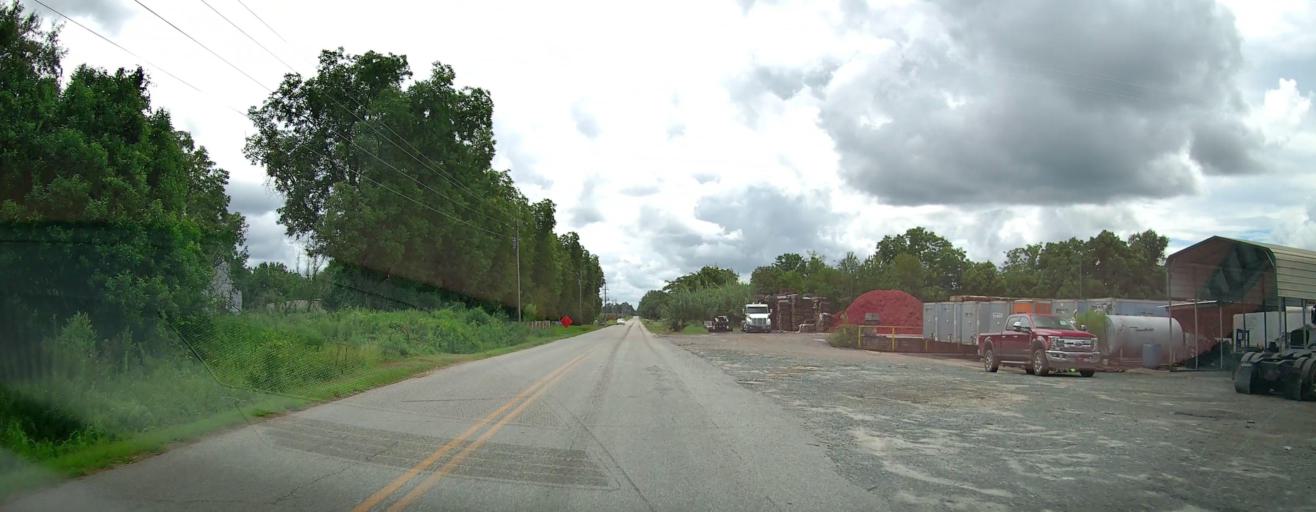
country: US
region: Georgia
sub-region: Peach County
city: Byron
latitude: 32.6067
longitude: -83.7480
